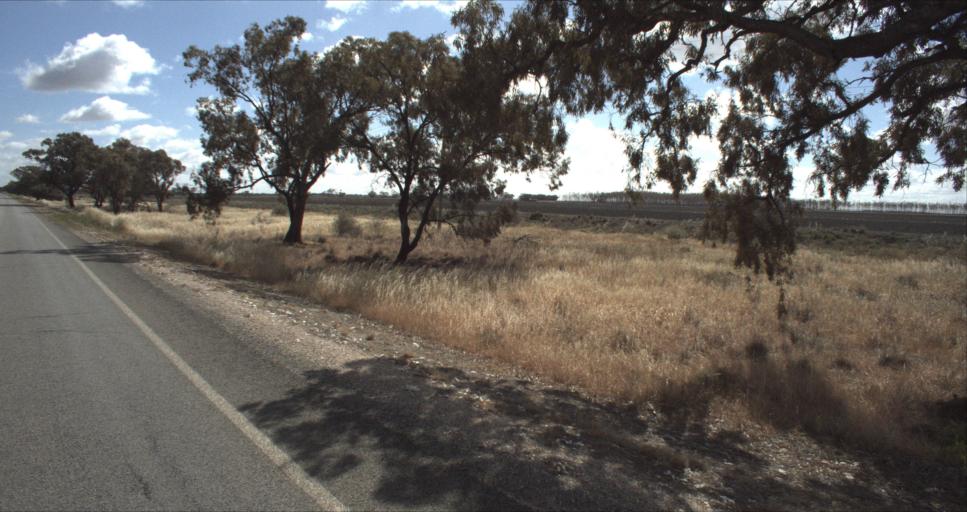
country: AU
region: New South Wales
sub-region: Murrumbidgee Shire
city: Darlington Point
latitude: -34.5645
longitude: 146.1684
